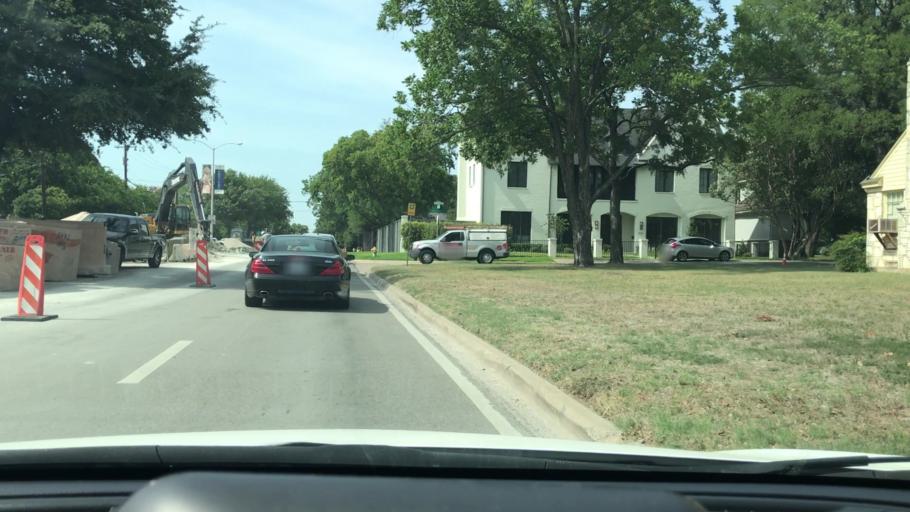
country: US
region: Texas
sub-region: Dallas County
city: University Park
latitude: 32.8839
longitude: -96.8039
